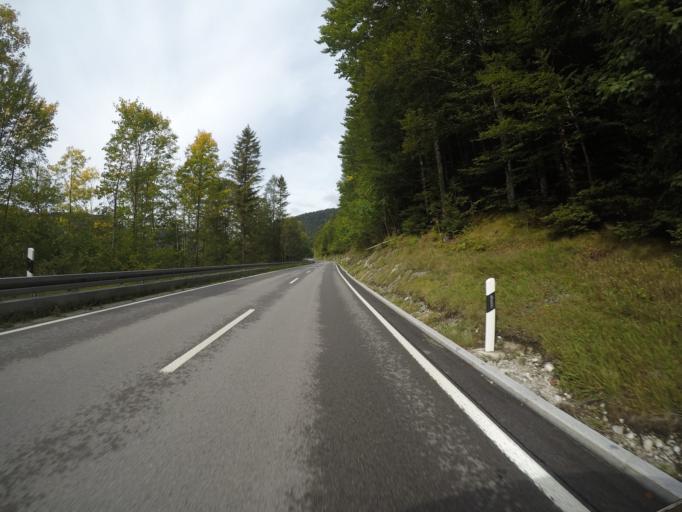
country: DE
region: Bavaria
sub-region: Upper Bavaria
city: Lenggries
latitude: 47.5825
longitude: 11.5834
